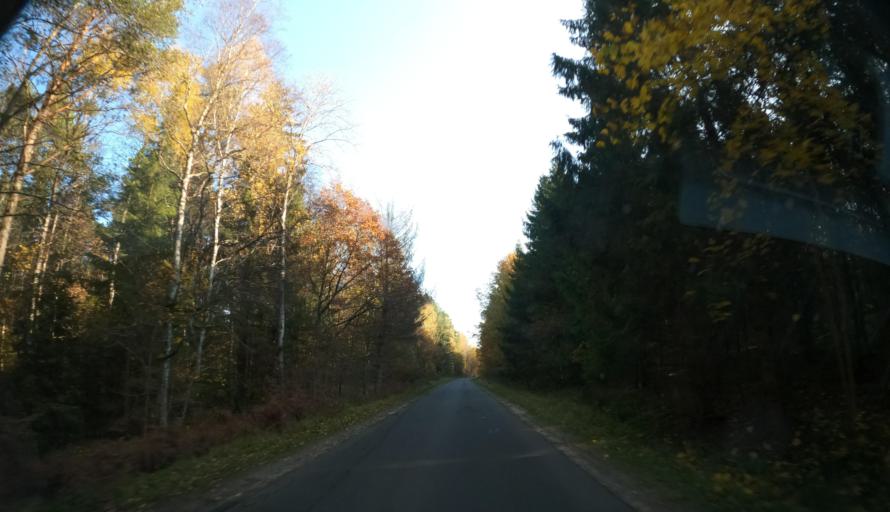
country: PL
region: Pomeranian Voivodeship
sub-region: Powiat slupski
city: Kepice
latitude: 54.2299
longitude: 16.7737
